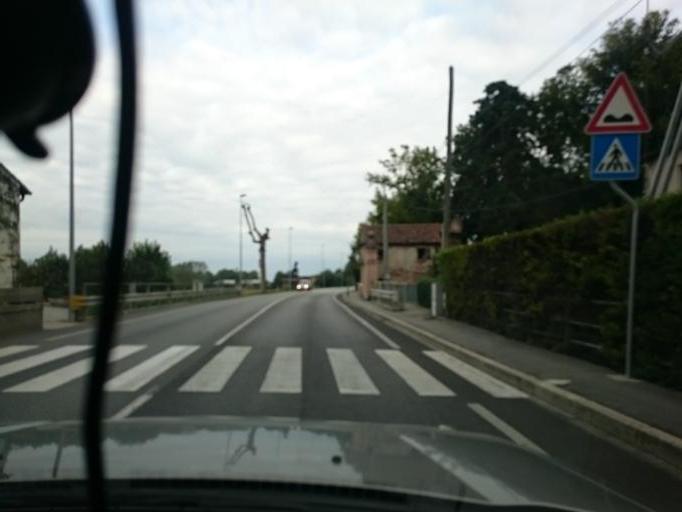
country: IT
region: Veneto
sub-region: Provincia di Padova
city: Arlesega
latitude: 45.4614
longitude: 11.7176
